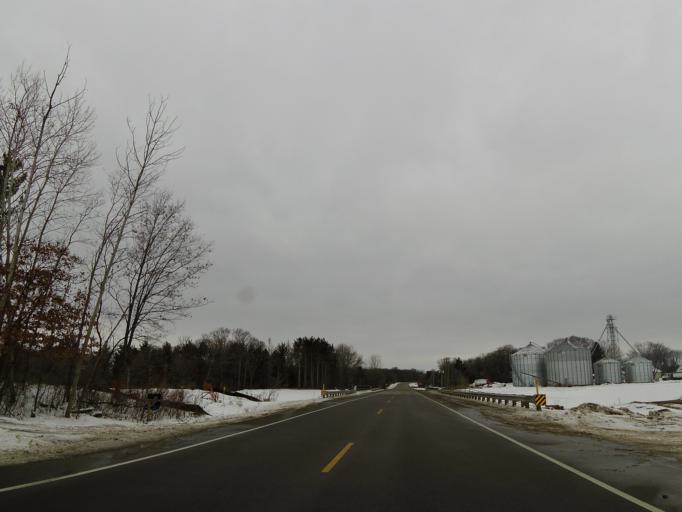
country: US
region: Minnesota
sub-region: Washington County
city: Oak Park Heights
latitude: 45.0466
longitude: -92.7794
